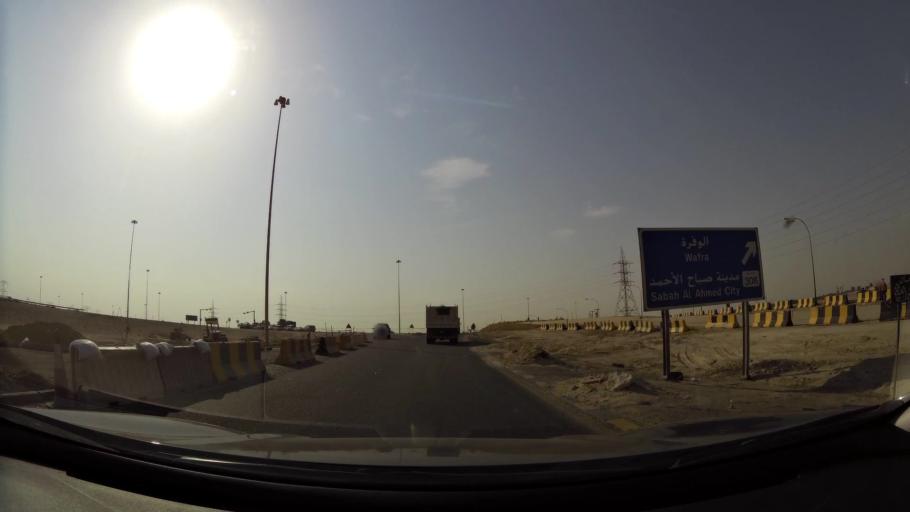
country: KW
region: Al Ahmadi
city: Al Ahmadi
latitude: 28.9594
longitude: 48.1206
